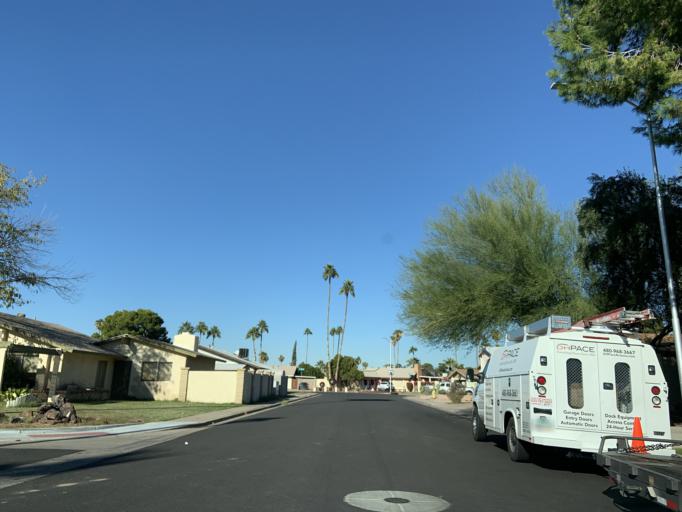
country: US
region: Arizona
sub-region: Maricopa County
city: Tempe
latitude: 33.3975
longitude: -111.8773
